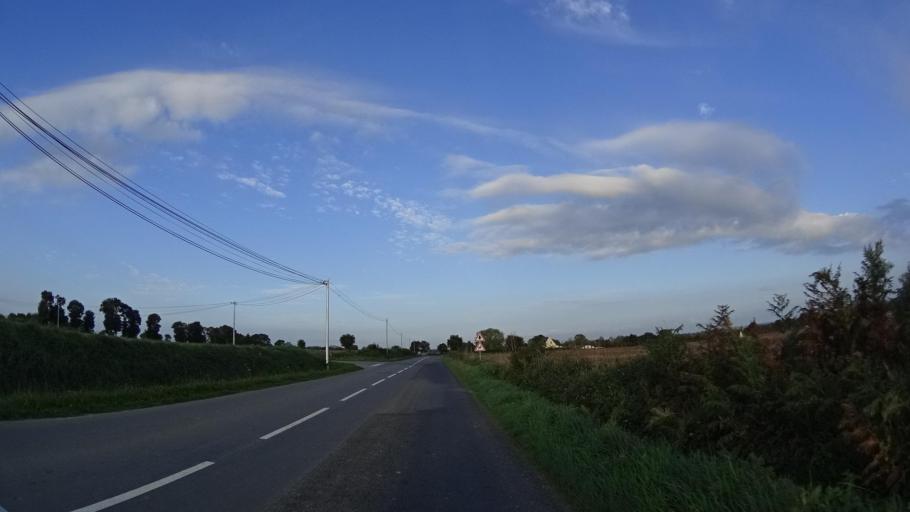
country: FR
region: Brittany
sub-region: Departement des Cotes-d'Armor
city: Plouasne
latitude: 48.2804
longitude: -2.0023
